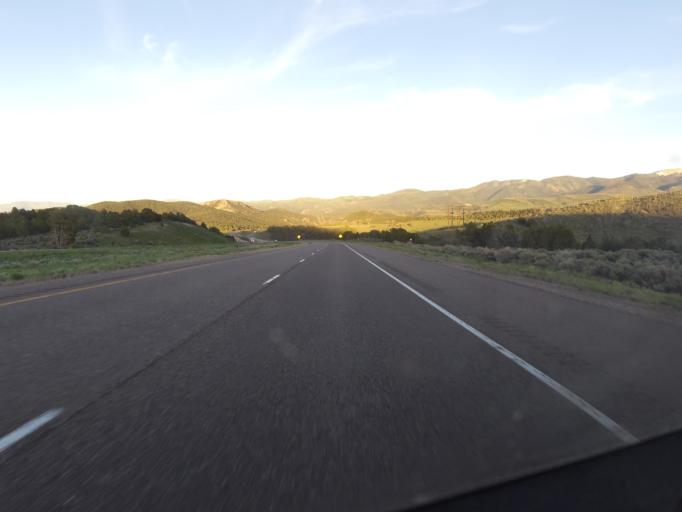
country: US
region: Utah
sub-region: Beaver County
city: Beaver
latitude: 38.5755
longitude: -112.4703
